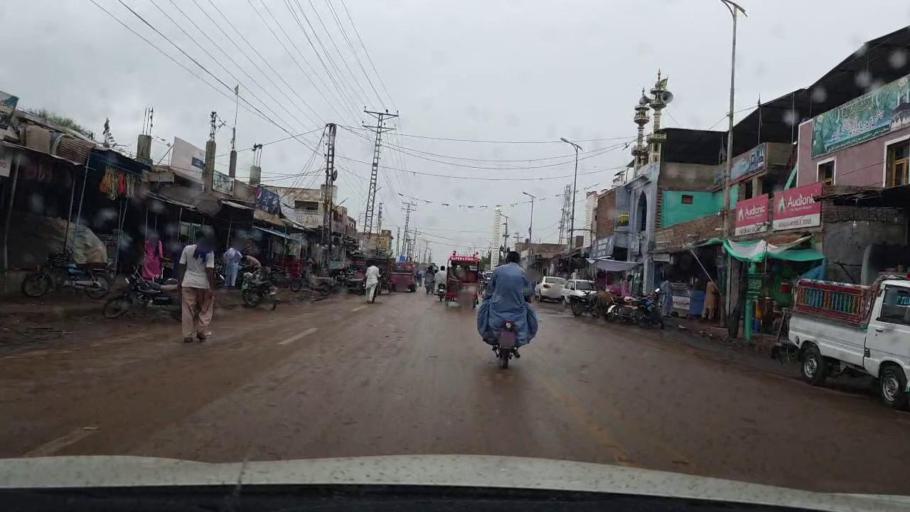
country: PK
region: Sindh
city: Kario
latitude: 24.6534
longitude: 68.5345
